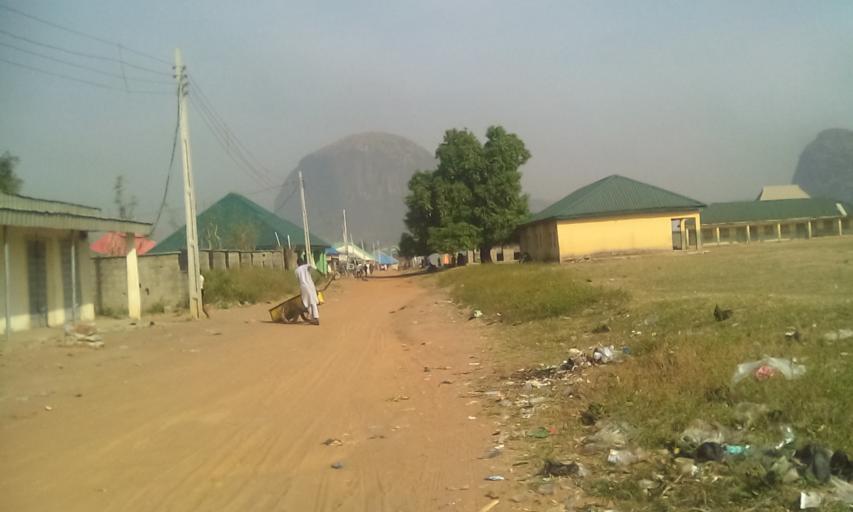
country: NG
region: Abuja Federal Capital Territory
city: Madala
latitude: 9.1073
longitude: 7.2421
